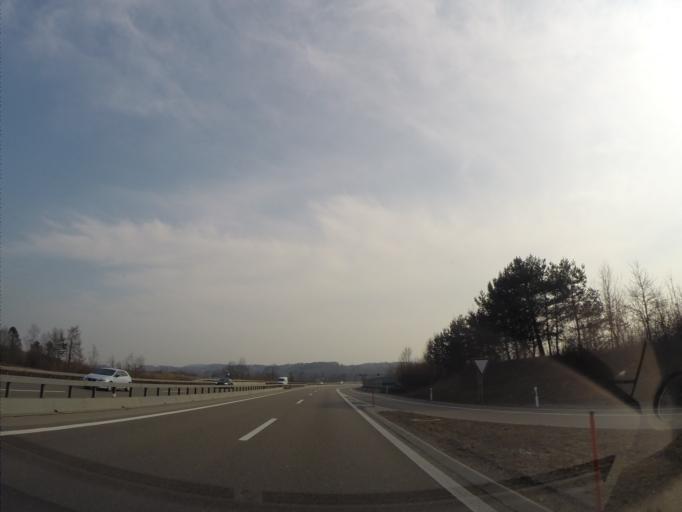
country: CH
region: Zurich
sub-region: Bezirk Andelfingen
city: Kleinandelfingen
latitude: 47.6035
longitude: 8.6896
